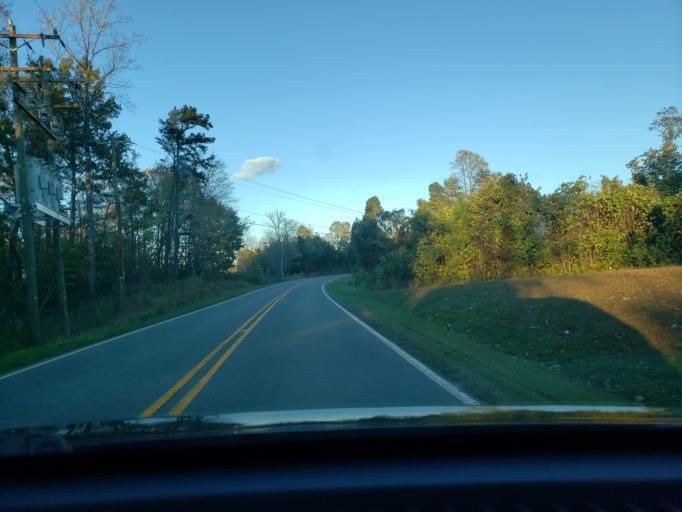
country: US
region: North Carolina
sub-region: Stokes County
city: Danbury
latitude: 36.3614
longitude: -80.2081
